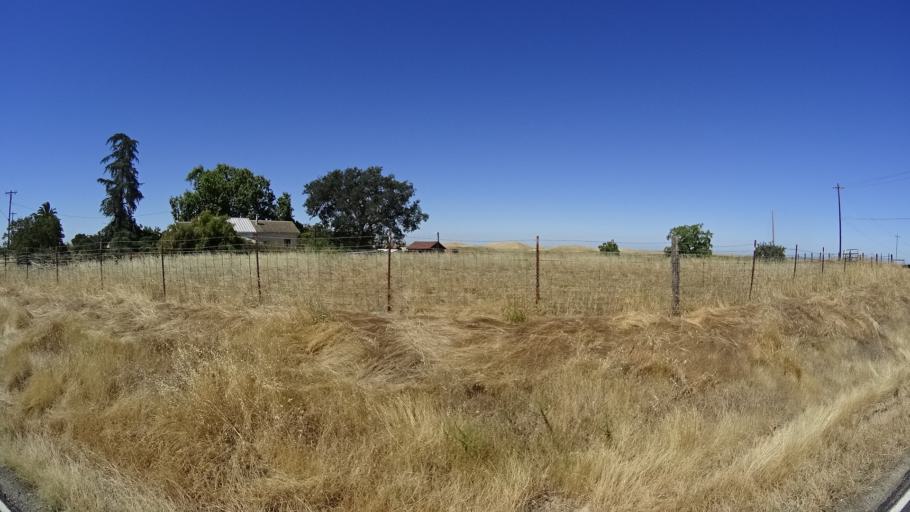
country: US
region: California
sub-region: Calaveras County
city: Rancho Calaveras
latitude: 38.0350
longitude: -120.8518
